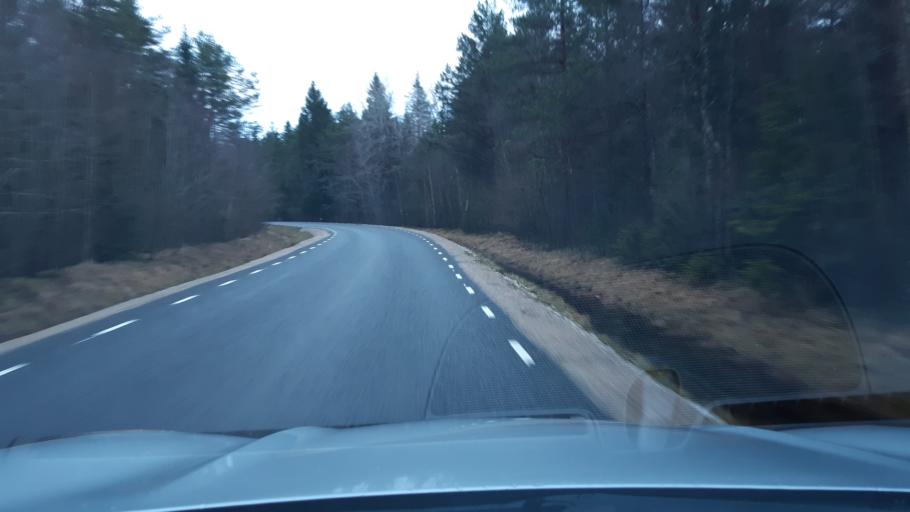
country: EE
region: Harju
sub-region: Saku vald
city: Saku
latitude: 59.1884
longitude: 24.6027
